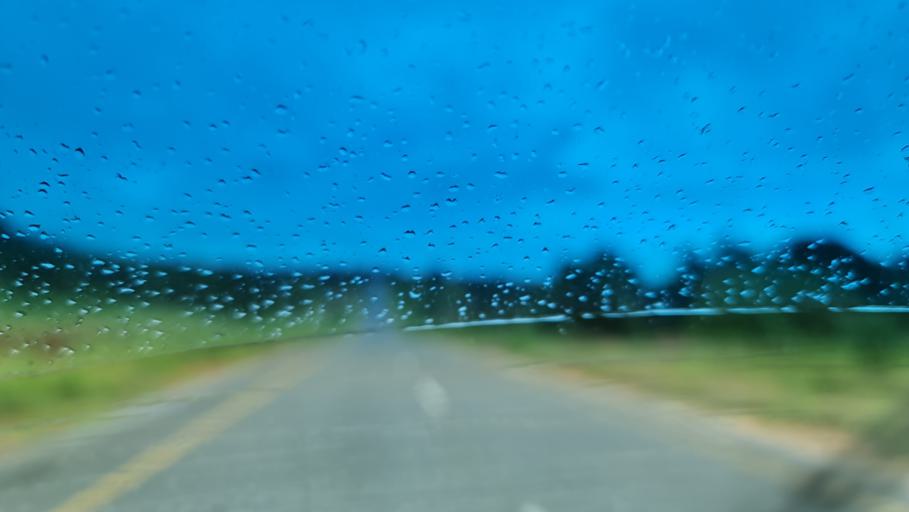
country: MZ
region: Nampula
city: Nampula
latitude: -15.4933
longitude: 39.3328
